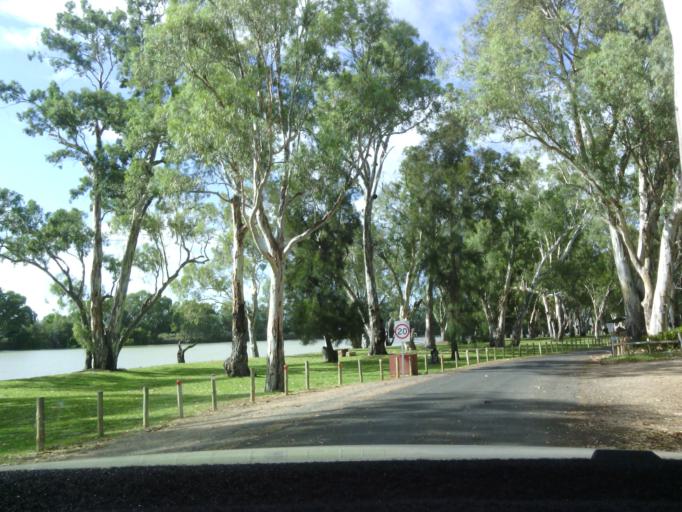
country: AU
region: South Australia
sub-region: Berri and Barmera
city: Berri
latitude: -34.2887
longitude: 140.6316
